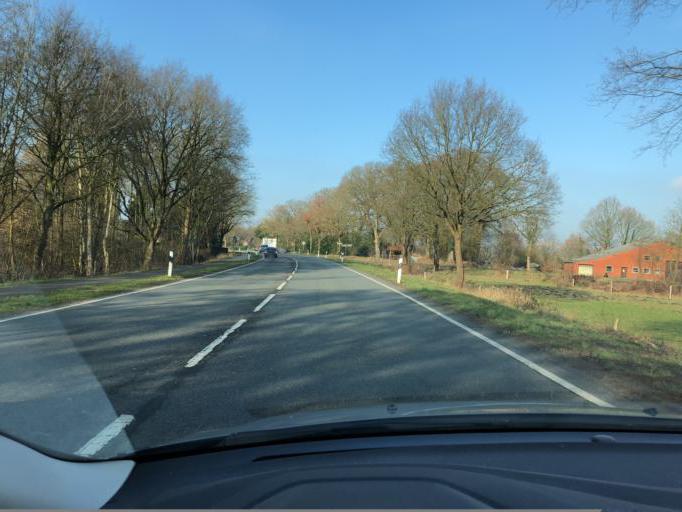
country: DE
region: Lower Saxony
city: Westerstede
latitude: 53.2904
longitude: 7.8871
